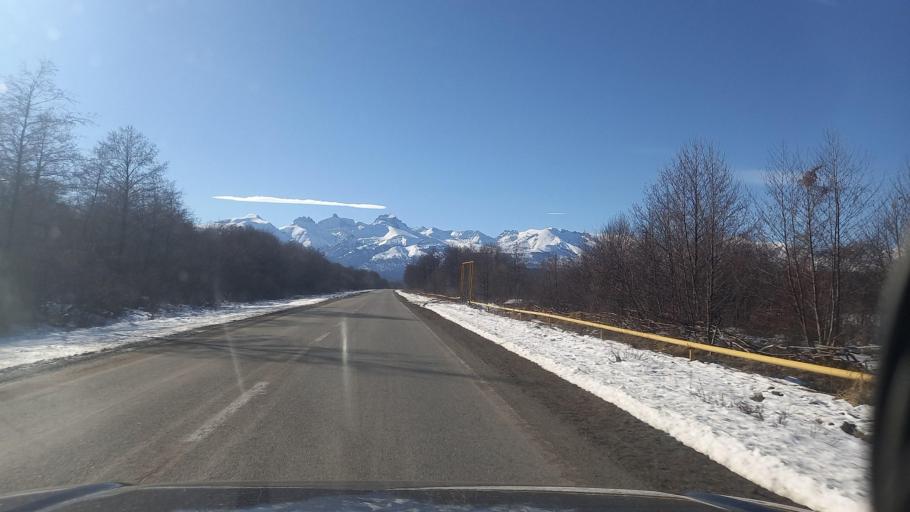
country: RU
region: North Ossetia
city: Chikola
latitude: 43.1574
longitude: 43.8468
